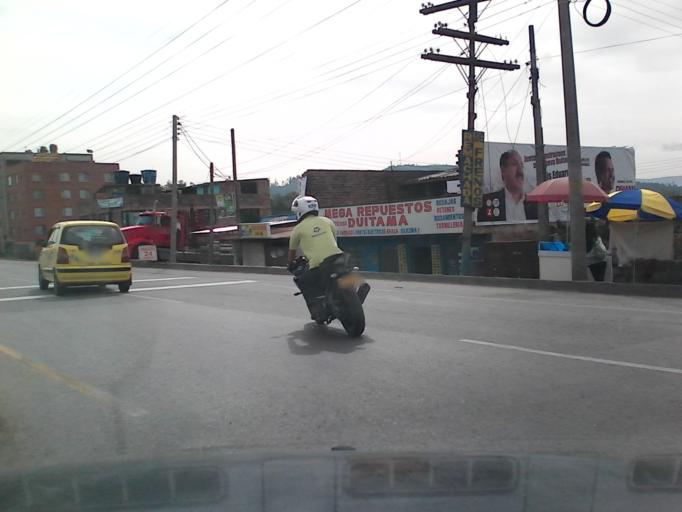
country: CO
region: Boyaca
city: Duitama
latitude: 5.8072
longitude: -73.0275
